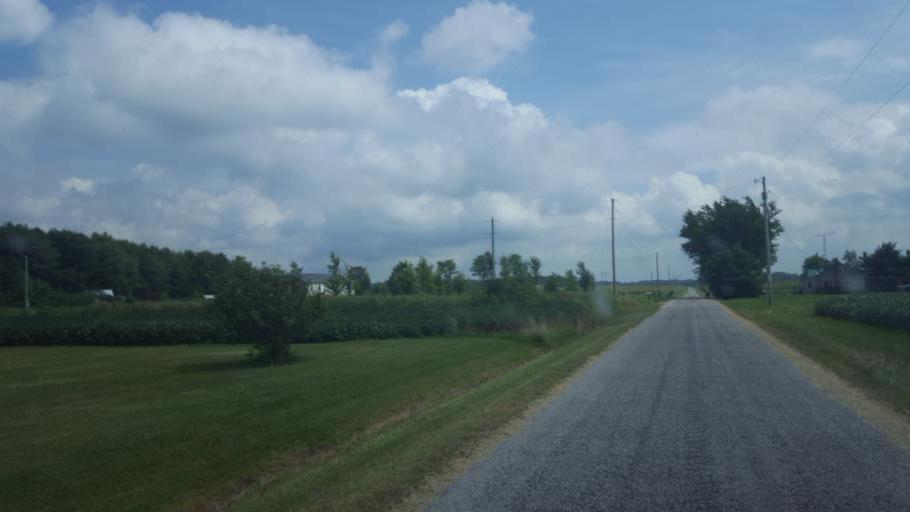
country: US
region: Ohio
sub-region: Richland County
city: Lexington
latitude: 40.6164
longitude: -82.7029
